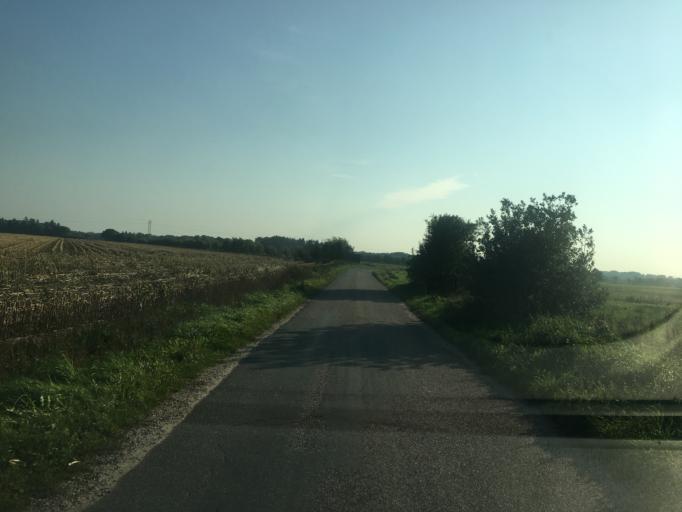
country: DE
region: Schleswig-Holstein
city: Bramstedtlund
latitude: 54.9678
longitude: 9.0701
